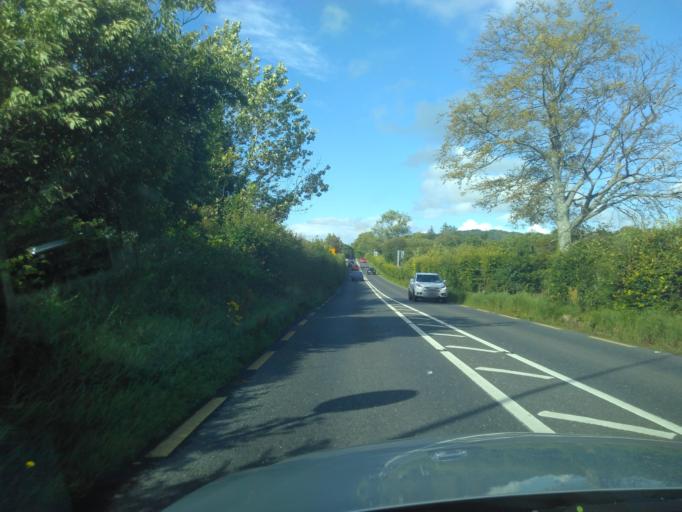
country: IE
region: Ulster
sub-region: County Donegal
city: Ballybofey
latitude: 54.8120
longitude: -7.7622
